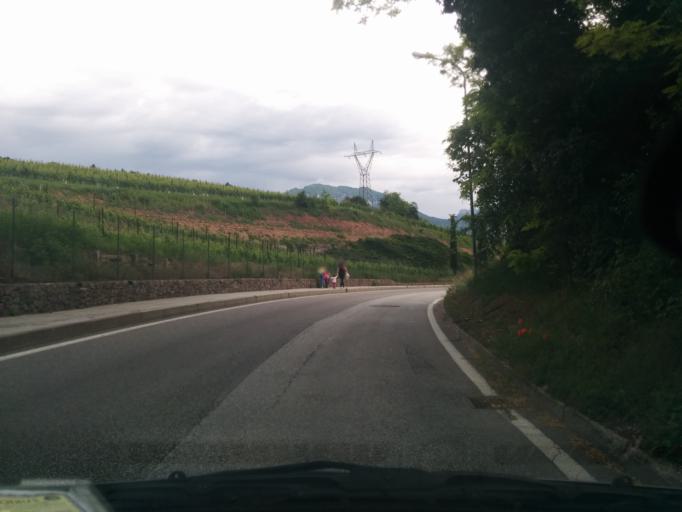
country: IT
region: Trentino-Alto Adige
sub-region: Provincia di Trento
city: Trento
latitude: 46.0917
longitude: 11.1336
